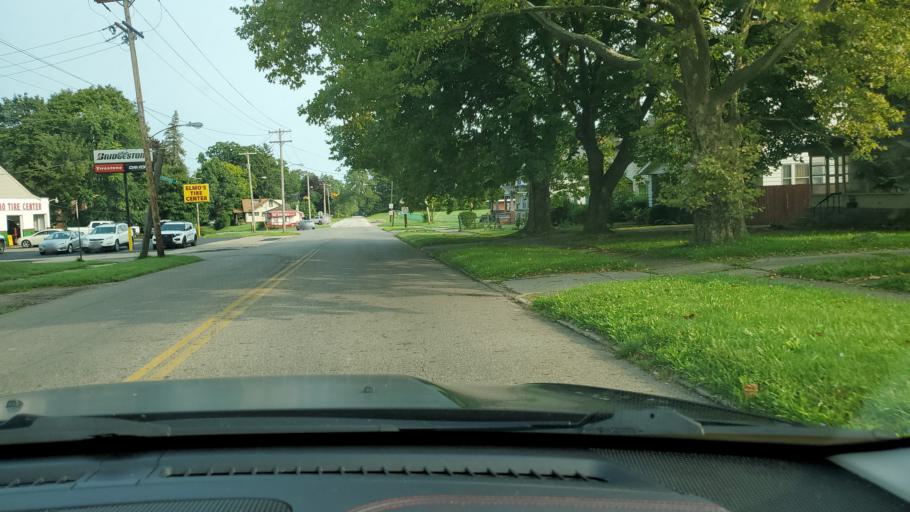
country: US
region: Ohio
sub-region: Mahoning County
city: Struthers
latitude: 41.0621
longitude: -80.6159
